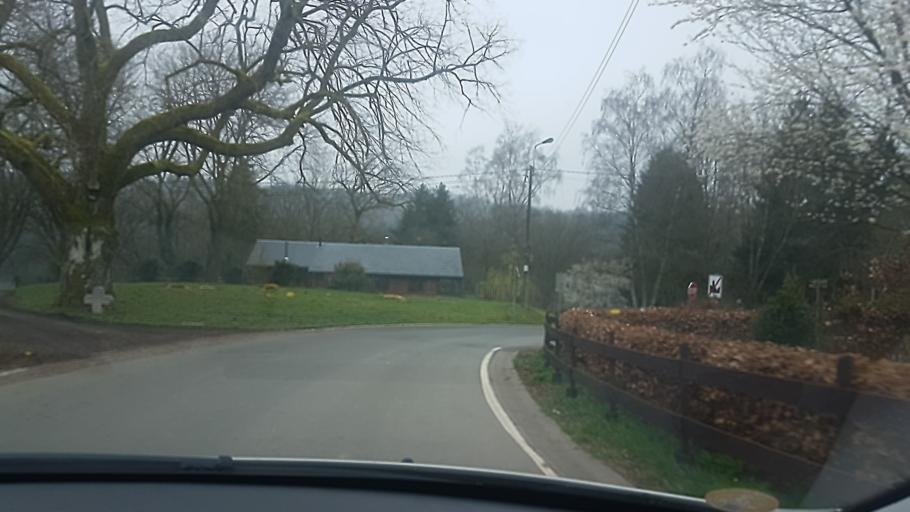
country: FR
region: Champagne-Ardenne
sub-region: Departement des Ardennes
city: Haybes
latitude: 50.0311
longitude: 4.6689
